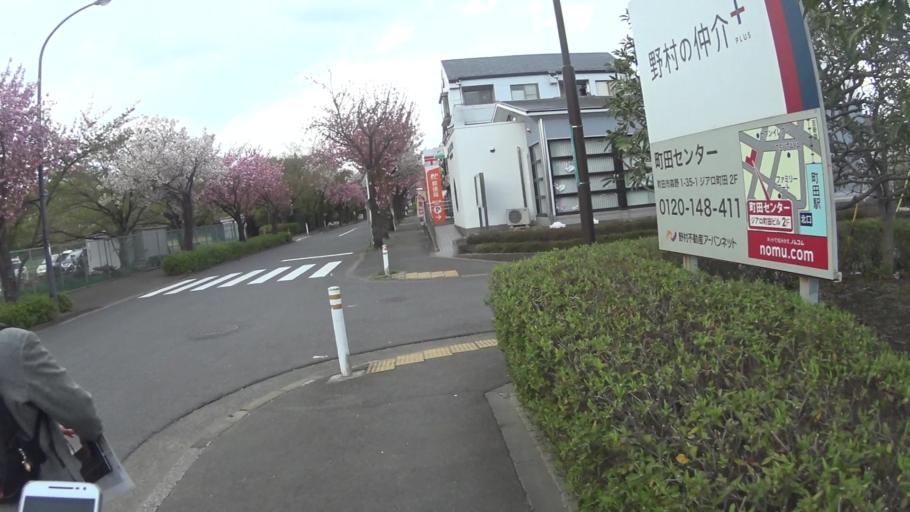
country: JP
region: Tokyo
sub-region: Machida-shi
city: Machida
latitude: 35.5737
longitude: 139.4889
